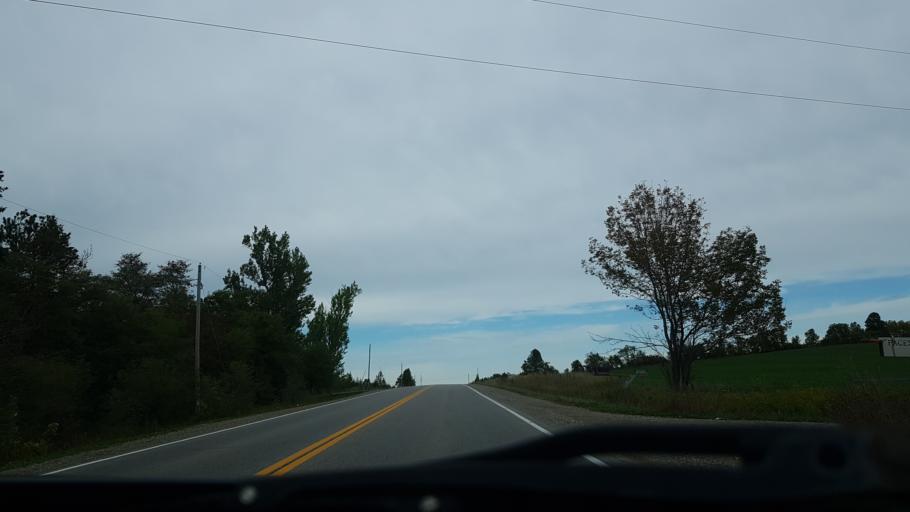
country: CA
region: Ontario
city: Shelburne
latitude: 44.0978
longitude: -80.0228
